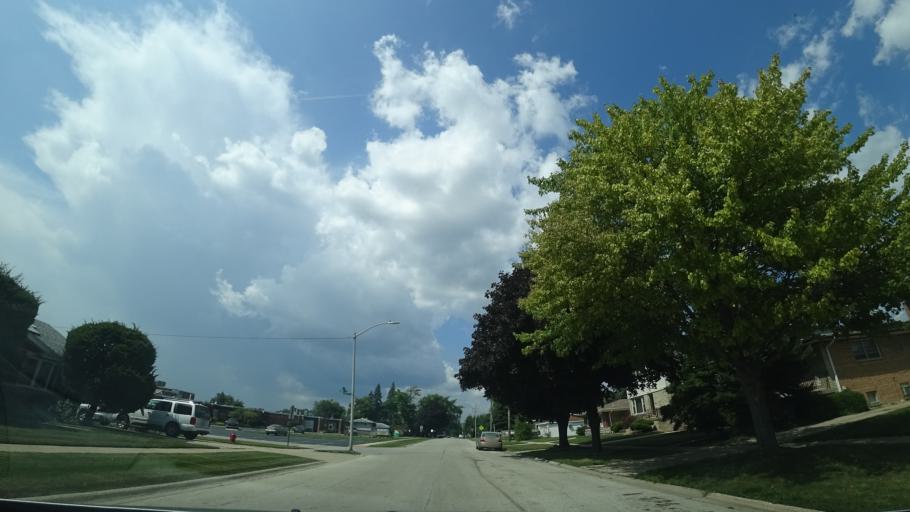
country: US
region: Illinois
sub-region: Cook County
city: Merrionette Park
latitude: 41.6709
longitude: -87.7148
